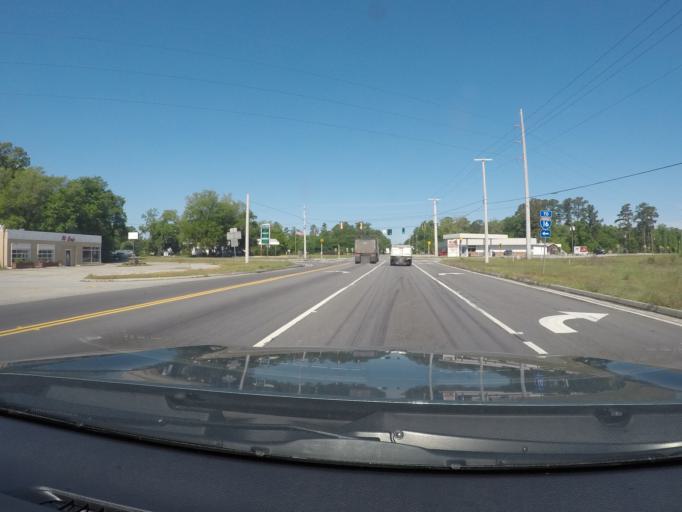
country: US
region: Georgia
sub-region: Effingham County
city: Guyton
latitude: 32.1968
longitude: -81.4374
